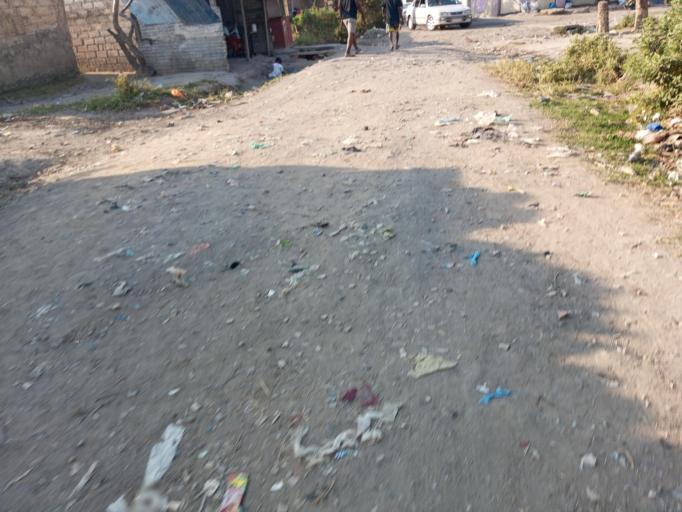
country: ZM
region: Lusaka
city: Lusaka
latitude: -15.3902
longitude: 28.2880
